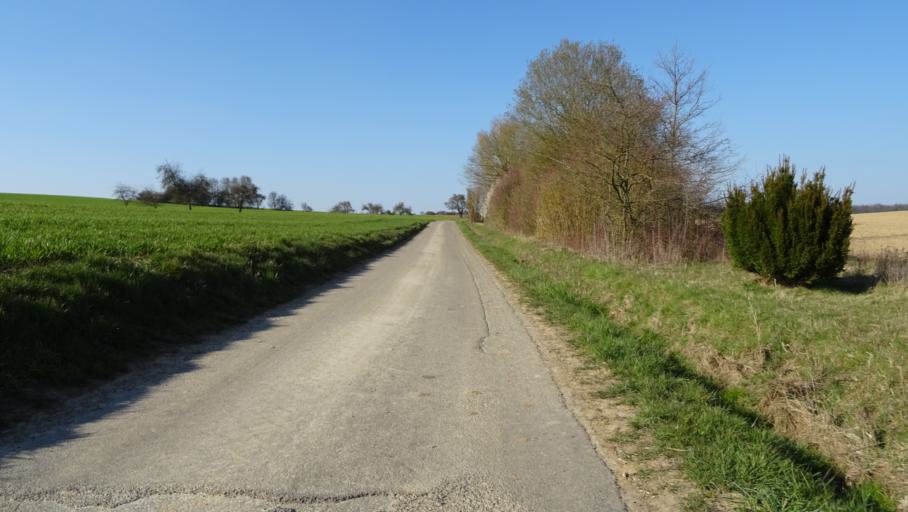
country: DE
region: Baden-Wuerttemberg
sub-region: Karlsruhe Region
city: Seckach
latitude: 49.4043
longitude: 9.2963
